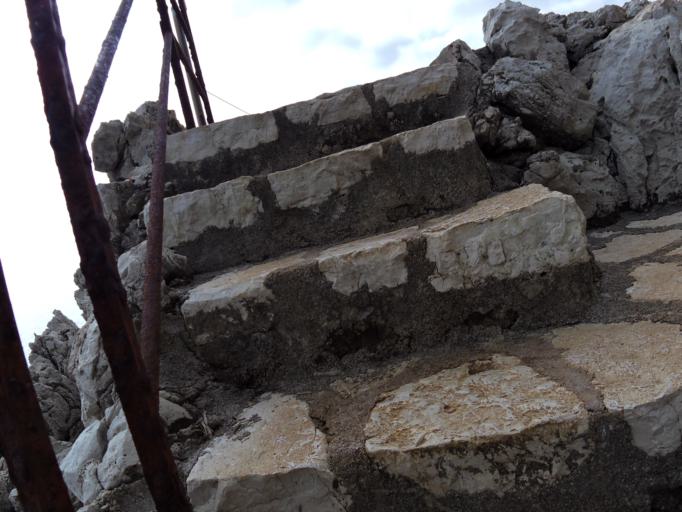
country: FR
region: Provence-Alpes-Cote d'Azur
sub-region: Departement des Alpes-Maritimes
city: Antibes
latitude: 43.5501
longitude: 7.1407
